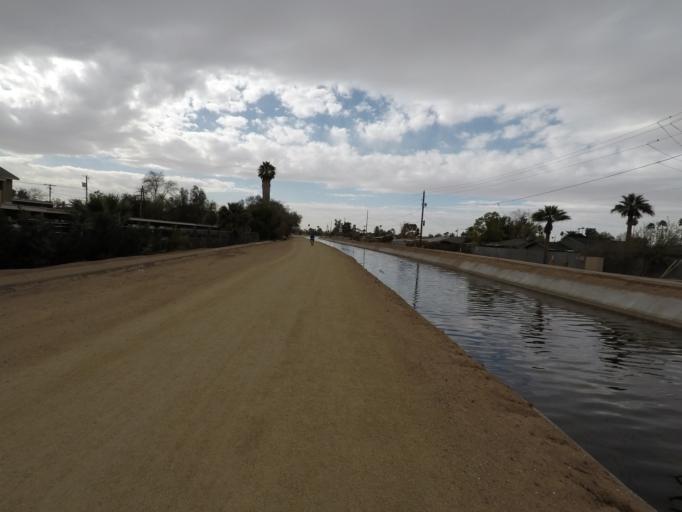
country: US
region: Arizona
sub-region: Maricopa County
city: Phoenix
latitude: 33.5024
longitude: -112.0841
